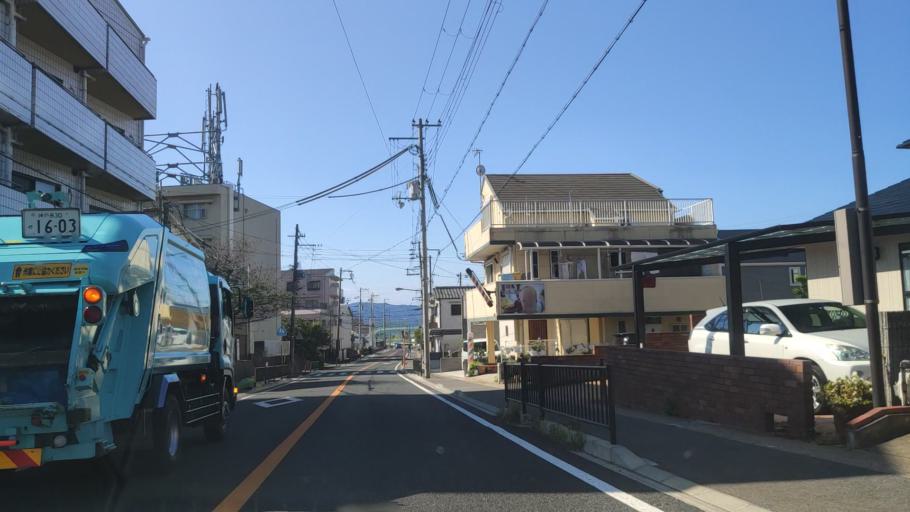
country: JP
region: Hyogo
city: Akashi
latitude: 34.6526
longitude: 135.0067
